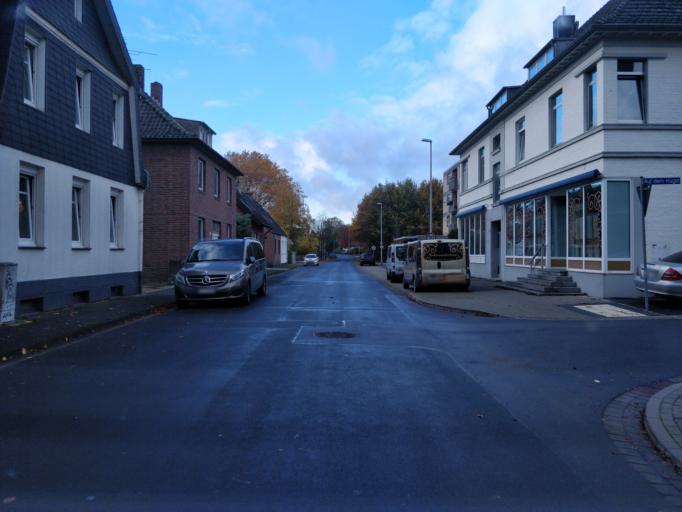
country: DE
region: North Rhine-Westphalia
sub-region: Regierungsbezirk Dusseldorf
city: Emmerich
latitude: 51.8481
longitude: 6.2534
